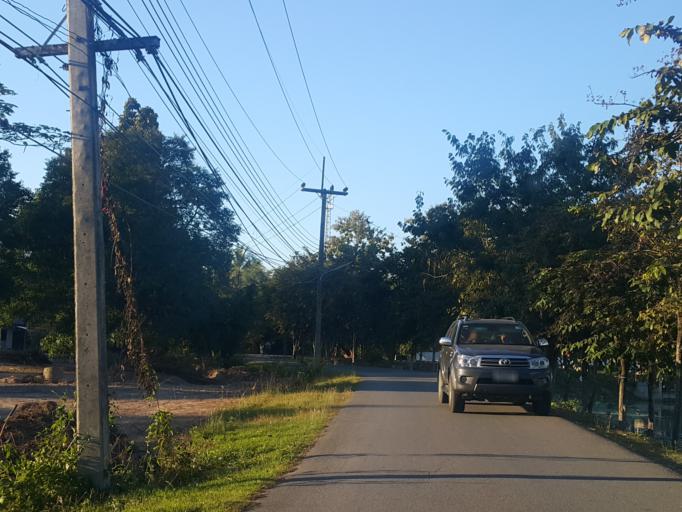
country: TH
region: Chiang Mai
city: San Sai
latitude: 18.8721
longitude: 99.1505
